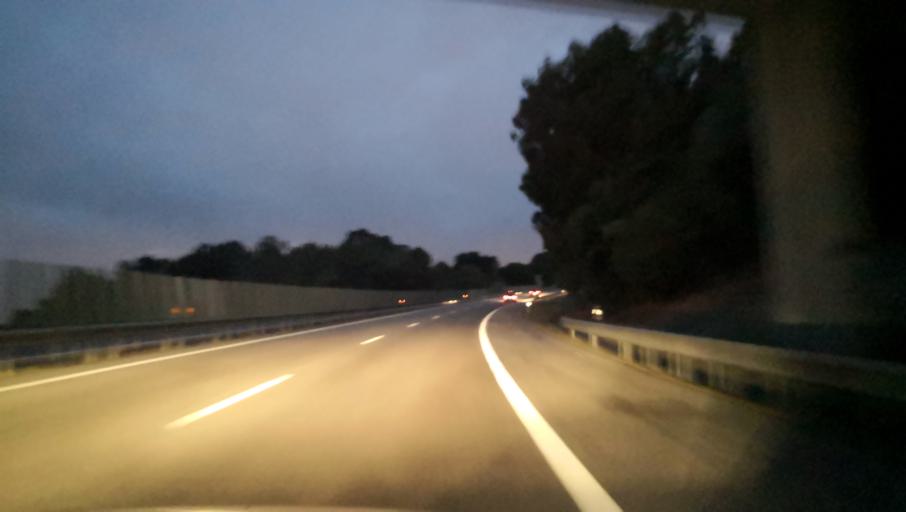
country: PT
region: Setubal
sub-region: Barreiro
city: Santo Antonio da Charneca
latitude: 38.6318
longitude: -9.0430
